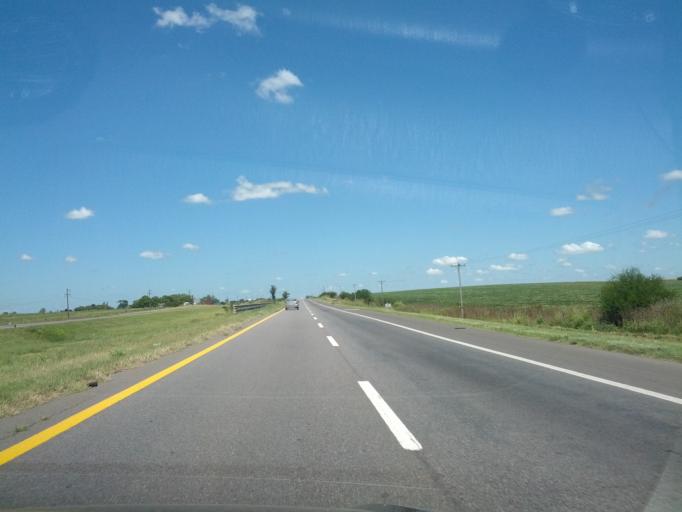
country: AR
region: Entre Rios
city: Gualeguaychu
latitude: -33.0785
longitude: -58.6350
